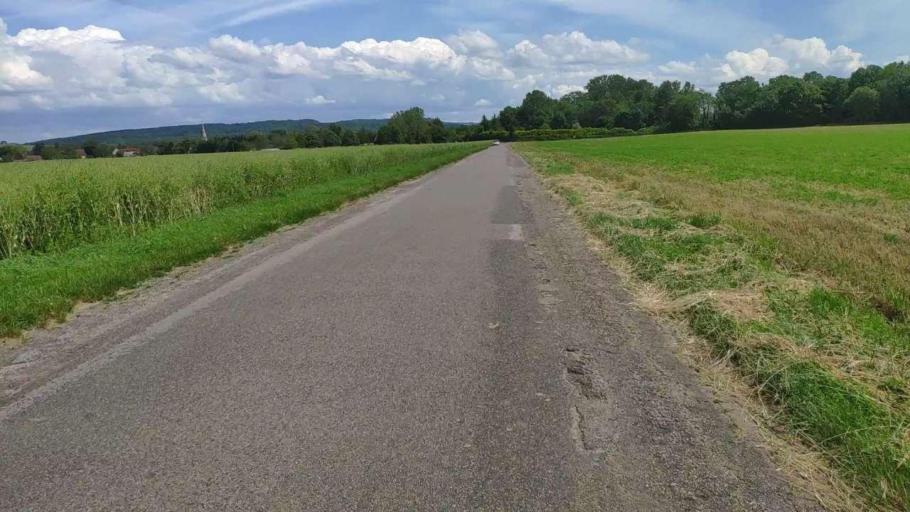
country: FR
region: Franche-Comte
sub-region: Departement du Jura
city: Bletterans
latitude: 46.7473
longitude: 5.4818
